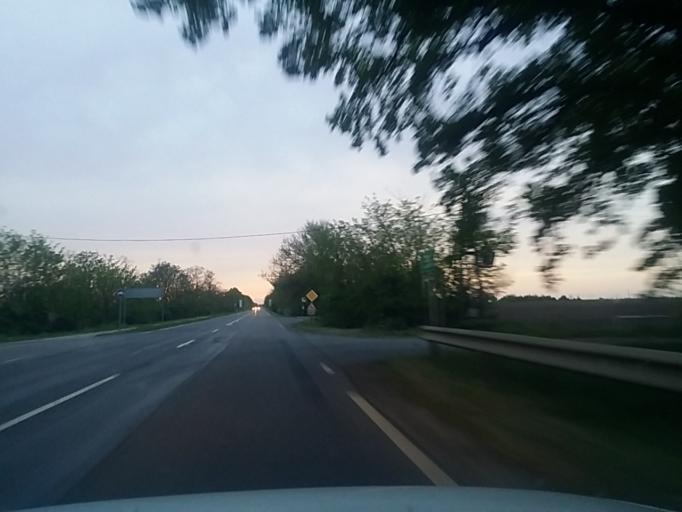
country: HU
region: Bekes
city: Csorvas
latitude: 46.7161
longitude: 20.9370
